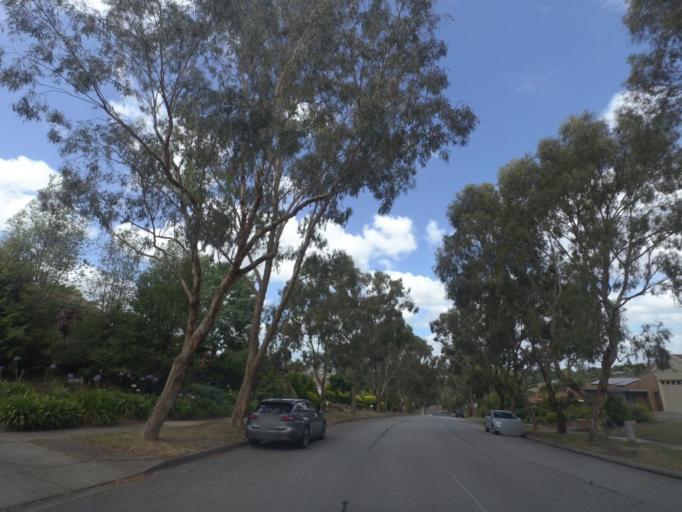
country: AU
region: Victoria
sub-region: Yarra Ranges
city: Lilydale
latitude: -37.7738
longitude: 145.3457
